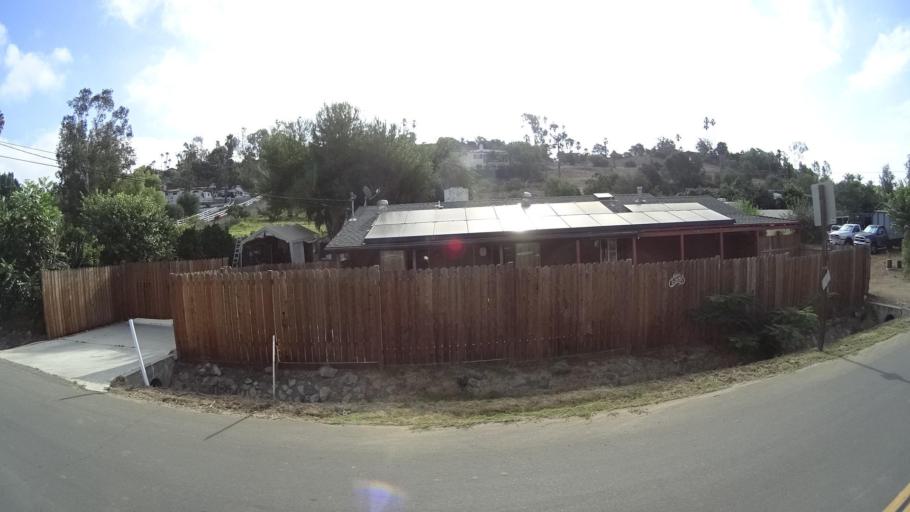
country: US
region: California
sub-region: San Diego County
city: Vista
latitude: 33.1953
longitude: -117.2119
